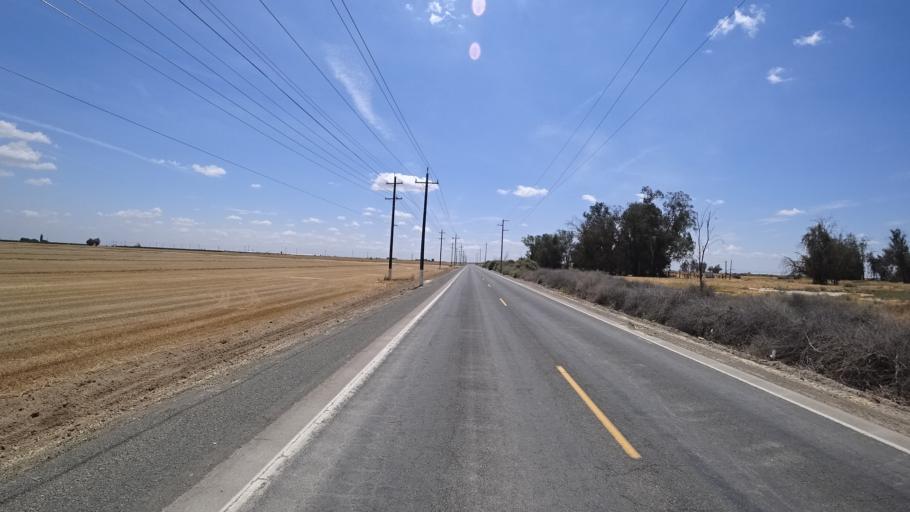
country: US
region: California
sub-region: Kings County
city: Home Garden
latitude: 36.2168
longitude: -119.6549
